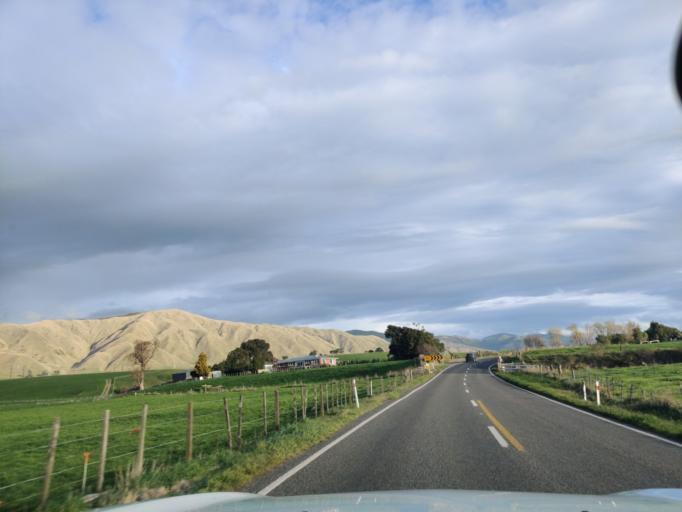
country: NZ
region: Manawatu-Wanganui
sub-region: Palmerston North City
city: Palmerston North
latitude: -40.4958
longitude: 175.4937
